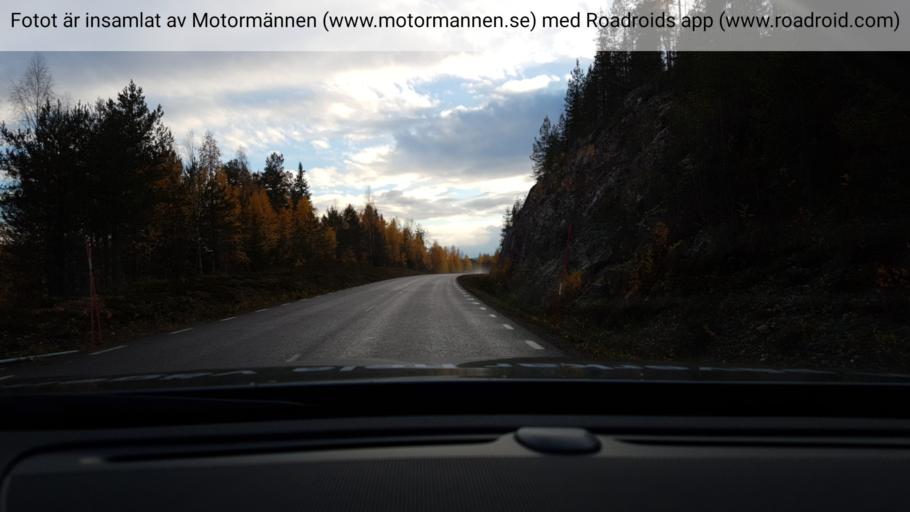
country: SE
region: Norrbotten
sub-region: Overkalix Kommun
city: OEverkalix
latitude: 66.7872
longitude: 22.7174
